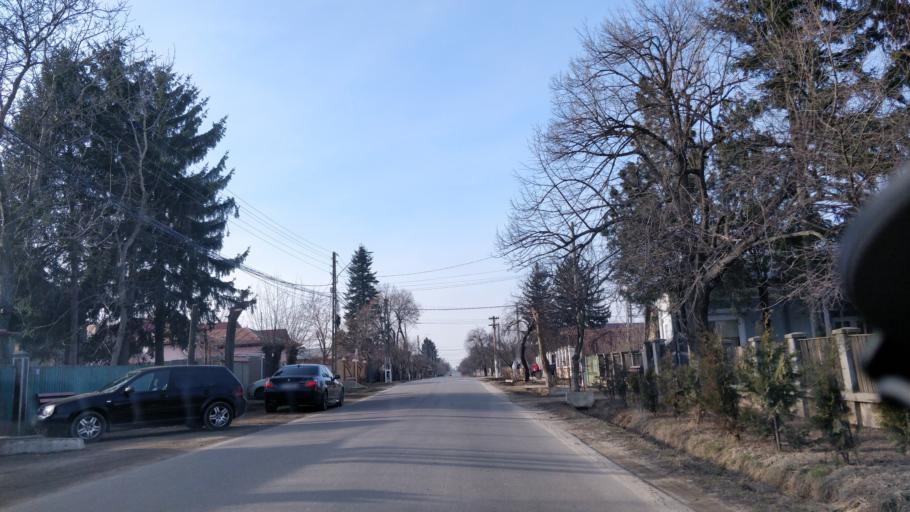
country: RO
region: Giurgiu
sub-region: Comuna Ulmi
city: Trestieni
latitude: 44.4976
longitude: 25.7701
